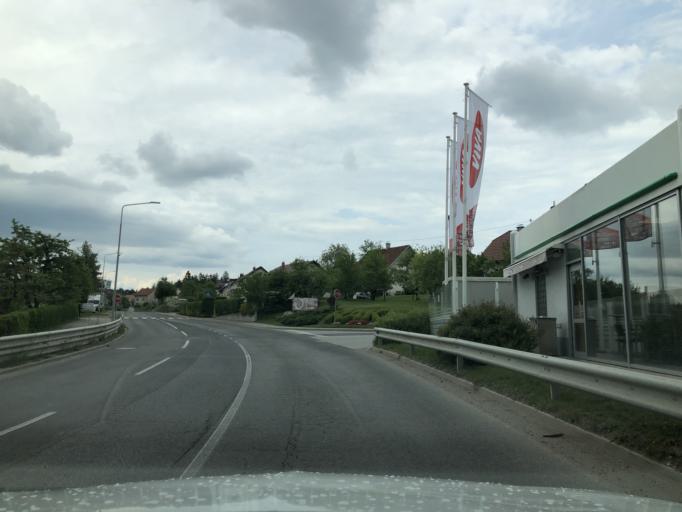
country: SI
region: Cerknica
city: Rakek
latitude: 45.8080
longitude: 14.3288
